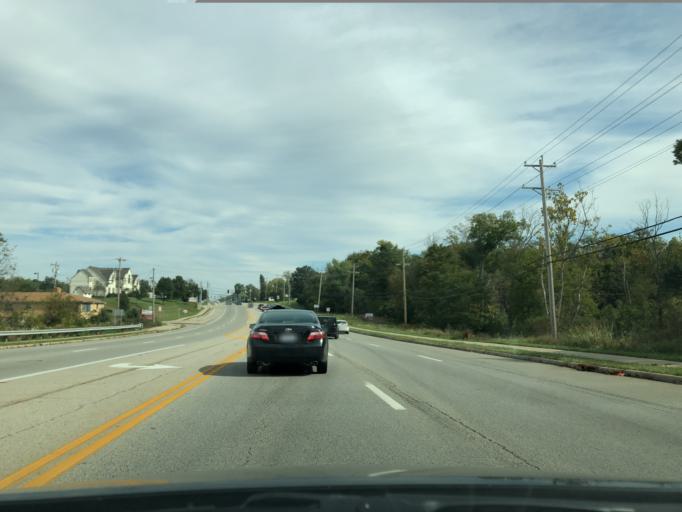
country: US
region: Ohio
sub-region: Clermont County
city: Mount Repose
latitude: 39.1966
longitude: -84.2316
